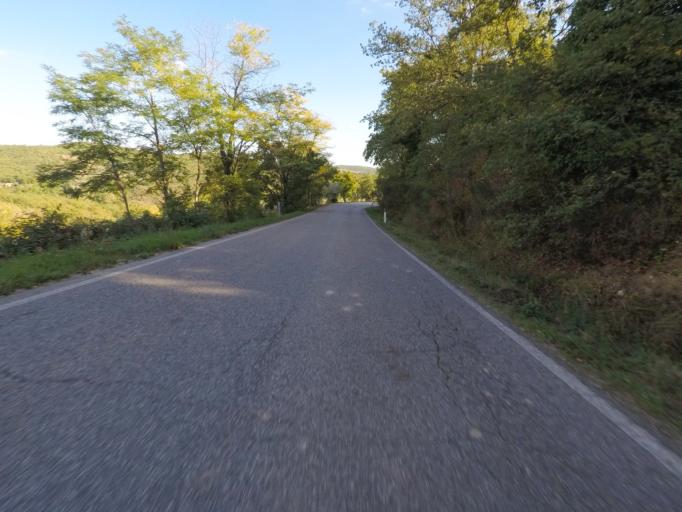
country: IT
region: Tuscany
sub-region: Provincia di Siena
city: Radda in Chianti
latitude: 43.4791
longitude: 11.3692
